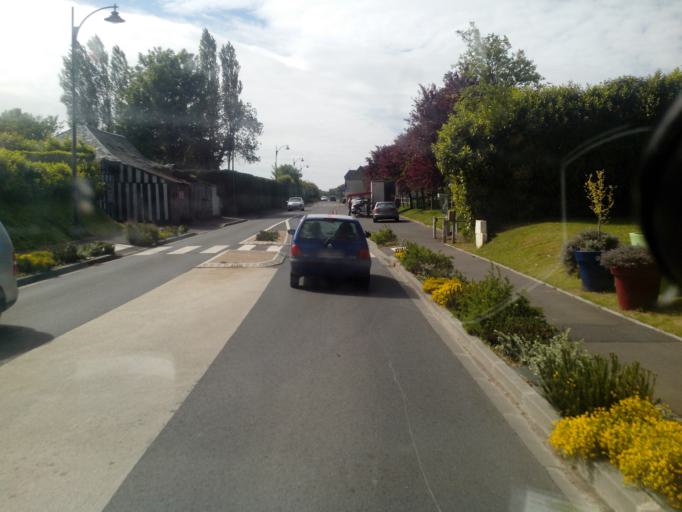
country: FR
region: Lower Normandy
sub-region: Departement du Calvados
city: Villers-sur-Mer
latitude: 49.2732
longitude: 0.0242
